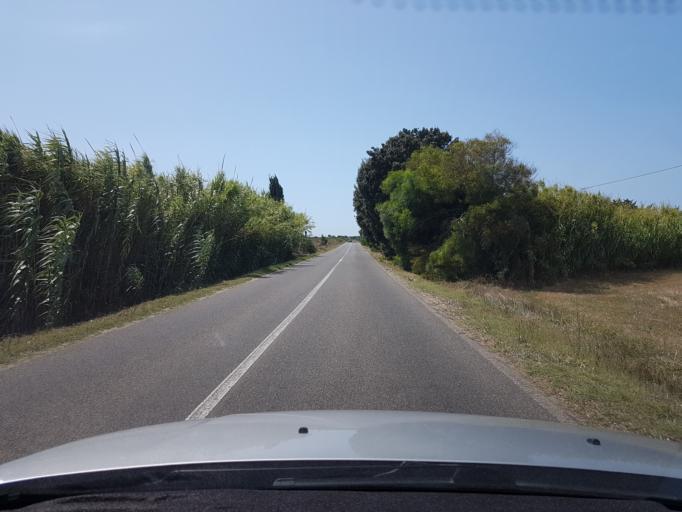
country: IT
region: Sardinia
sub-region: Provincia di Oristano
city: Riola Sardo
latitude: 40.0224
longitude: 8.4723
